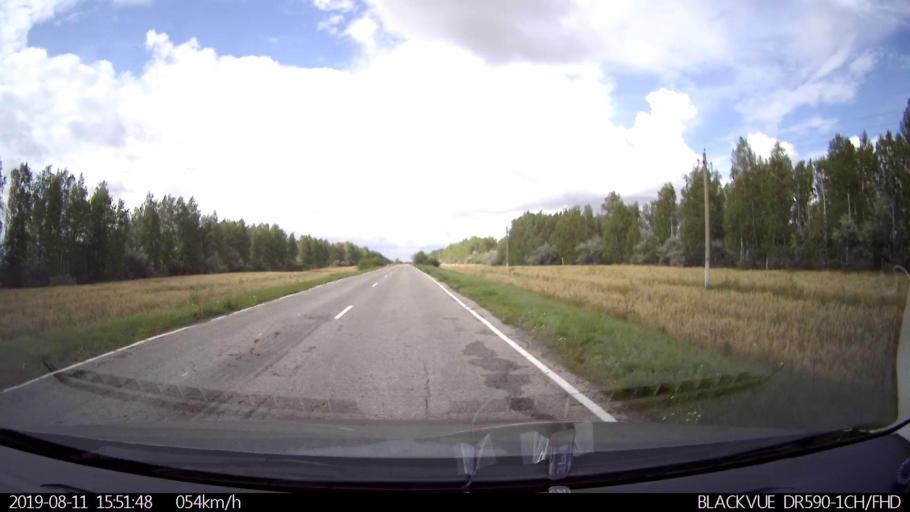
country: RU
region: Ulyanovsk
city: Ignatovka
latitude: 53.9217
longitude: 47.6562
